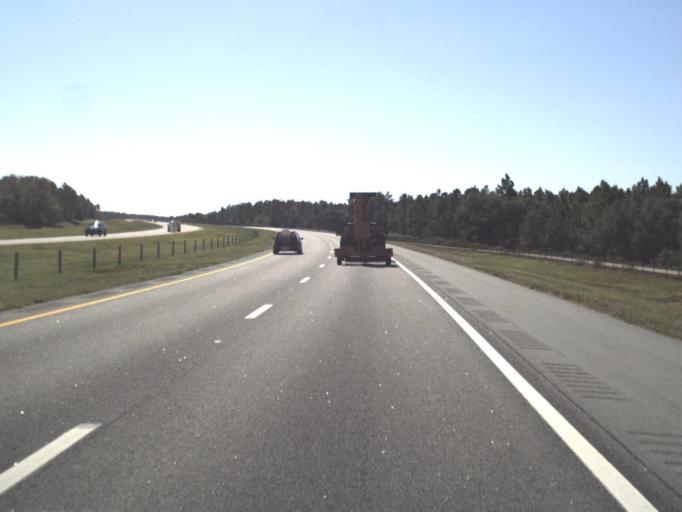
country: US
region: Florida
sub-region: Pasco County
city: Shady Hills
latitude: 28.3684
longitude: -82.5448
